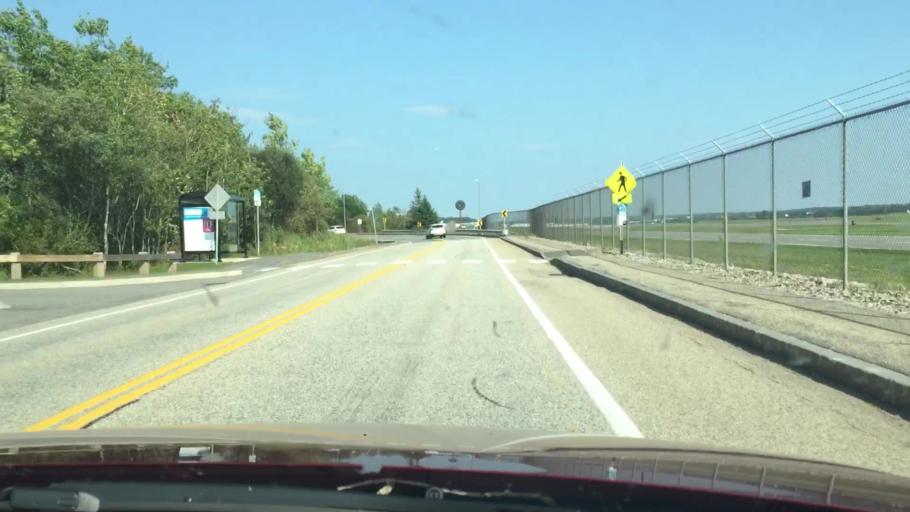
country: US
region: Maine
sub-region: Cumberland County
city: South Portland Gardens
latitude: 43.6473
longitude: -70.3195
